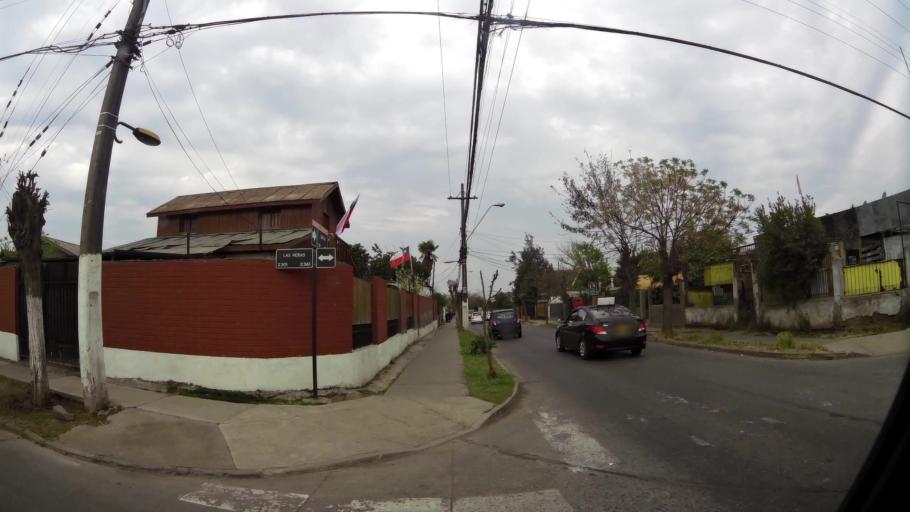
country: CL
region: Santiago Metropolitan
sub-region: Provincia de Santiago
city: Lo Prado
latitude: -33.5056
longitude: -70.7658
